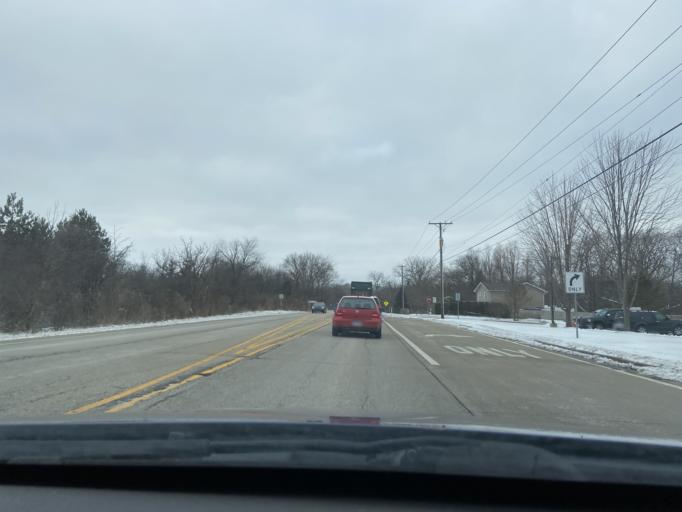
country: US
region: Illinois
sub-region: Lake County
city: Round Lake Park
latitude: 42.3711
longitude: -88.0669
